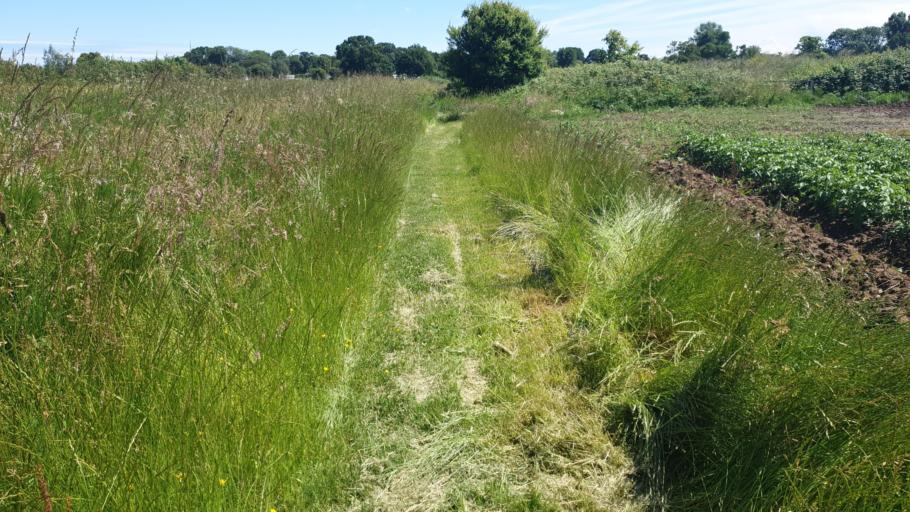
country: GB
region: England
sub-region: Essex
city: Saint Osyth
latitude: 51.7904
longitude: 1.1117
